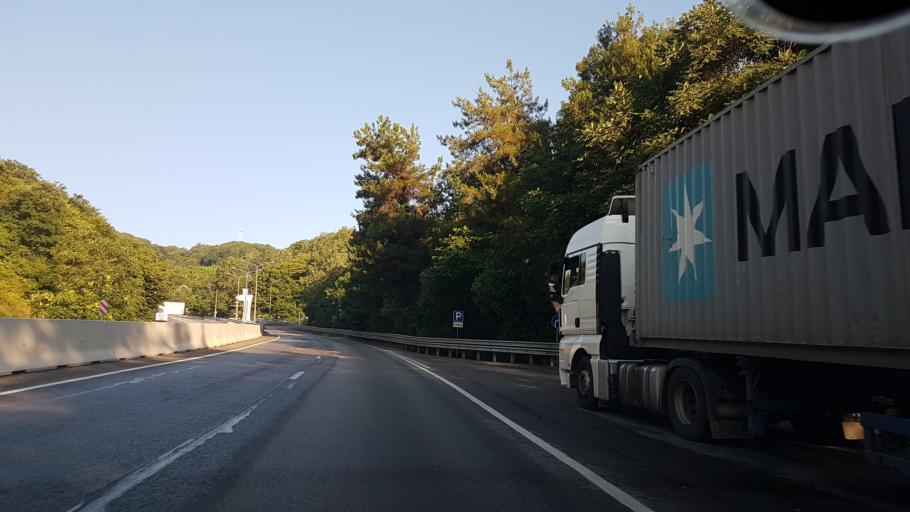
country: RU
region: Krasnodarskiy
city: Dagomys
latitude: 43.6442
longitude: 39.6987
